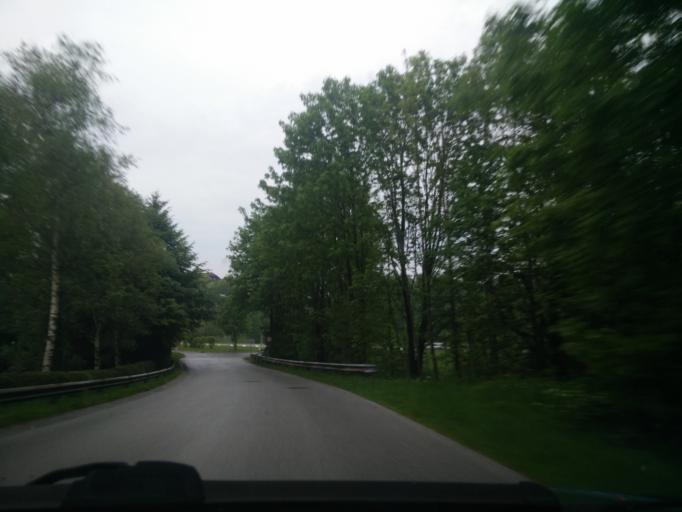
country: AT
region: Salzburg
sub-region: Politischer Bezirk Salzburg-Umgebung
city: Eugendorf
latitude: 47.8767
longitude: 13.1225
